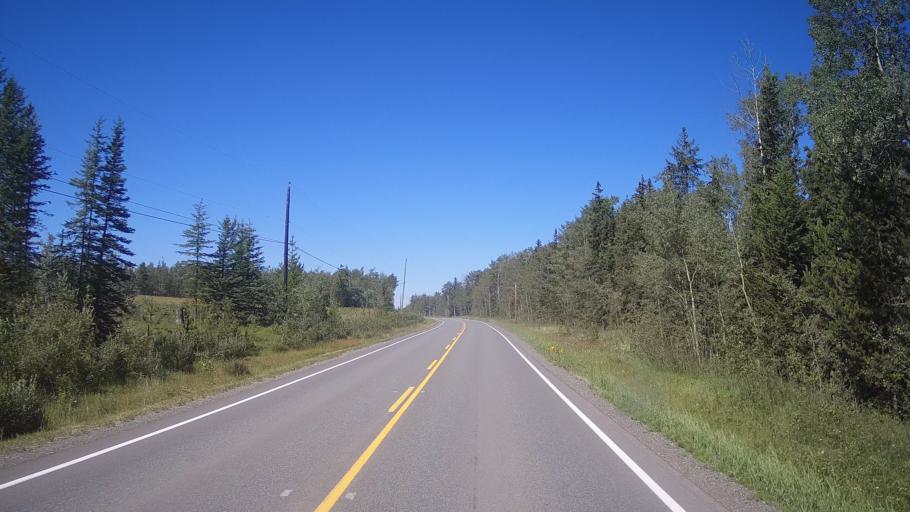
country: CA
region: British Columbia
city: Cache Creek
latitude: 51.5452
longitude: -120.9400
